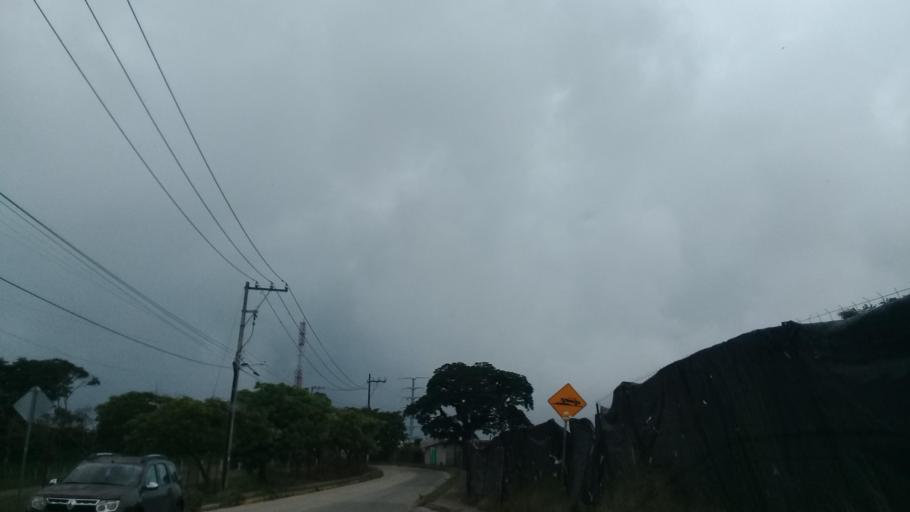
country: MX
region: Veracruz
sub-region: Emiliano Zapata
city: Las Trancas
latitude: 19.5051
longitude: -96.8657
